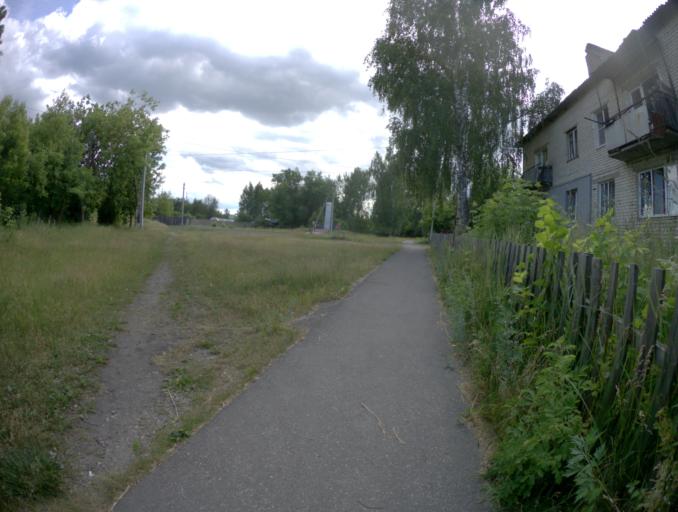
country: RU
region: Nizjnij Novgorod
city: Frolishchi
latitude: 56.4223
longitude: 42.6504
